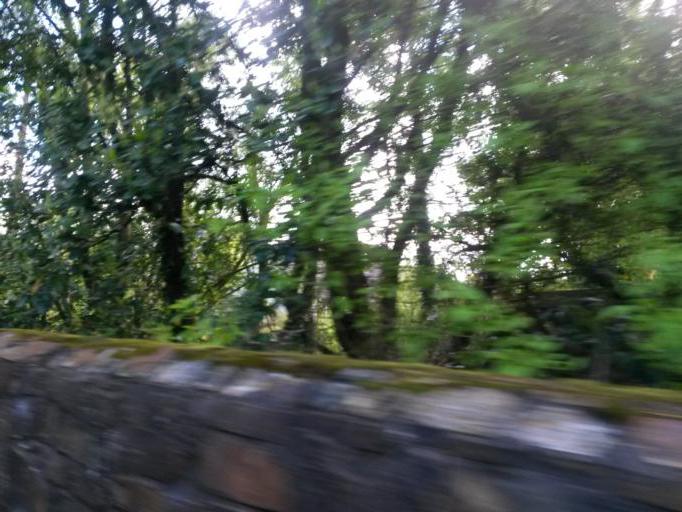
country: IE
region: Leinster
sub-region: Loch Garman
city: Enniscorthy
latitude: 52.4983
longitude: -6.5514
